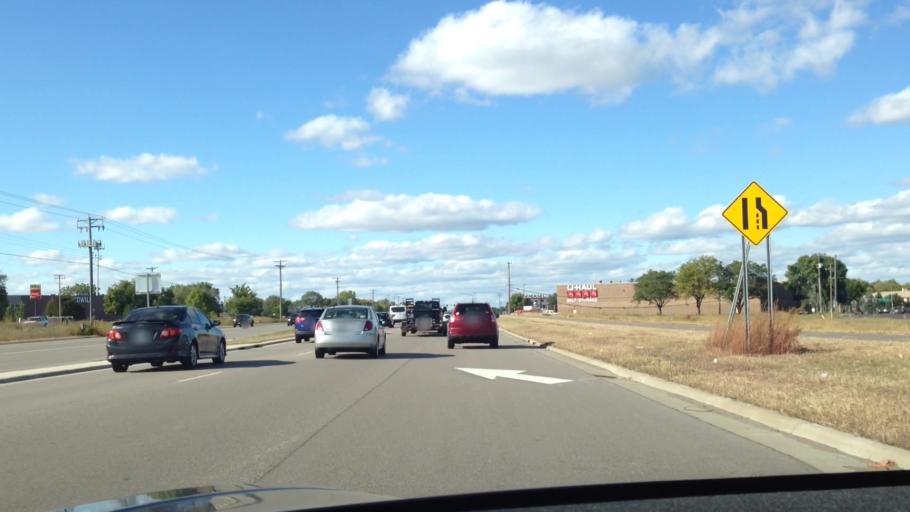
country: US
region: Minnesota
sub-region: Hennepin County
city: Brooklyn Park
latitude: 45.0799
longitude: -93.3747
